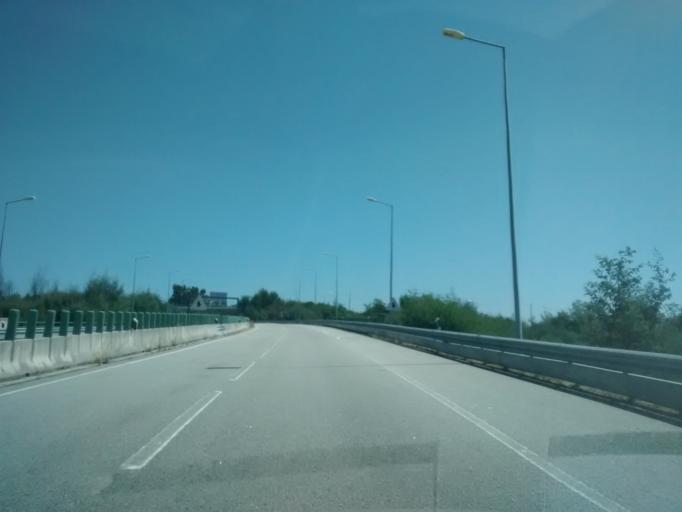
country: PT
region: Coimbra
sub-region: Tabua
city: Tabua
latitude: 40.3678
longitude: -8.0440
